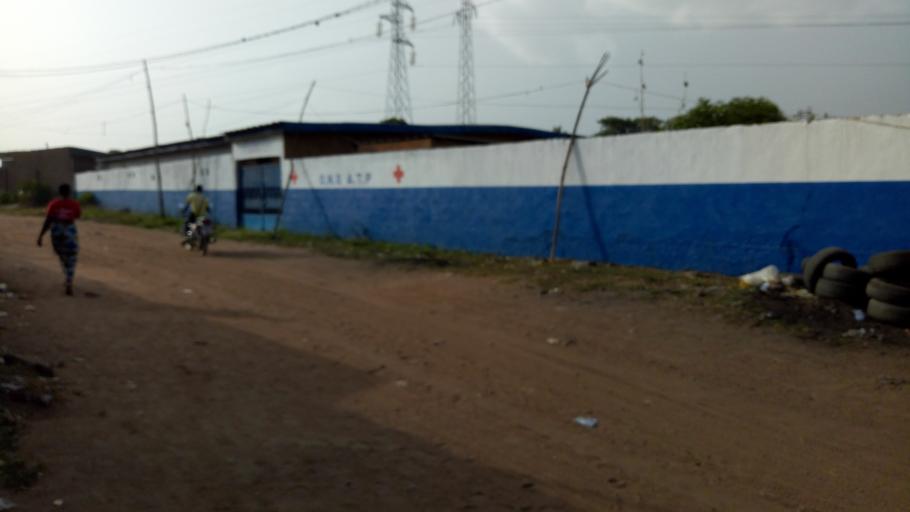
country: CI
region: Vallee du Bandama
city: Bouake
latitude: 7.6952
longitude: -5.0394
